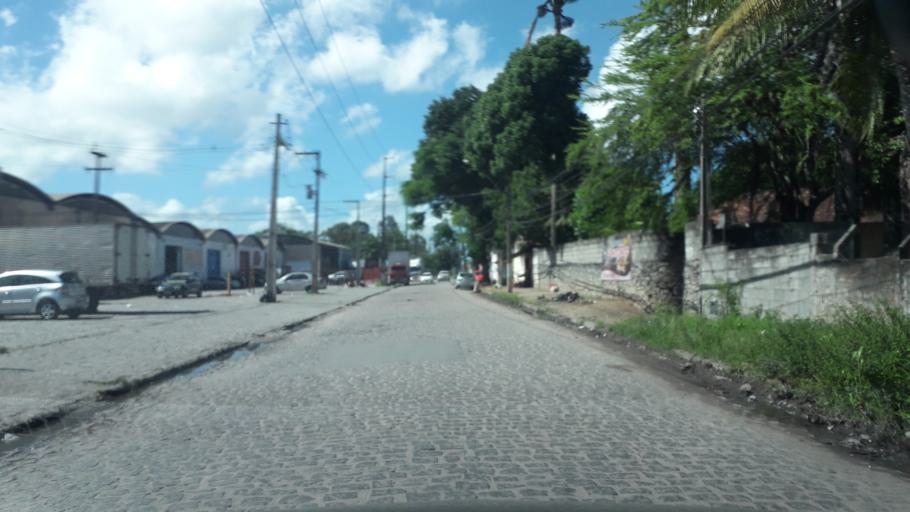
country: BR
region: Alagoas
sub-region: Satuba
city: Satuba
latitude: -9.5828
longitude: -35.7681
